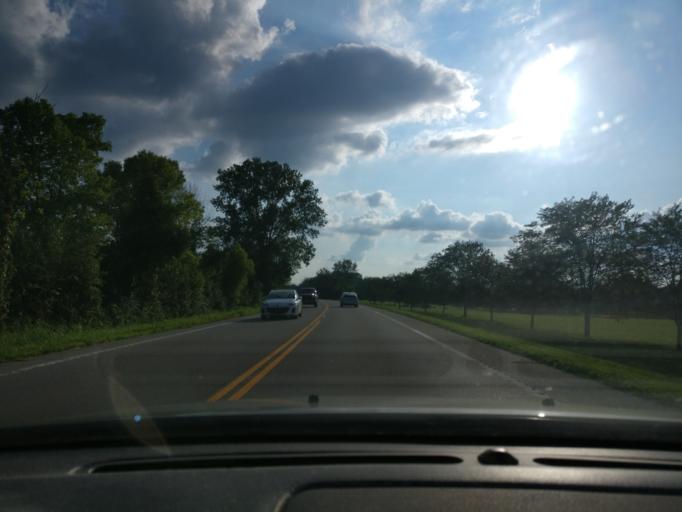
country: US
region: Ohio
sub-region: Warren County
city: Waynesville
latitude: 39.5207
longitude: -84.0647
